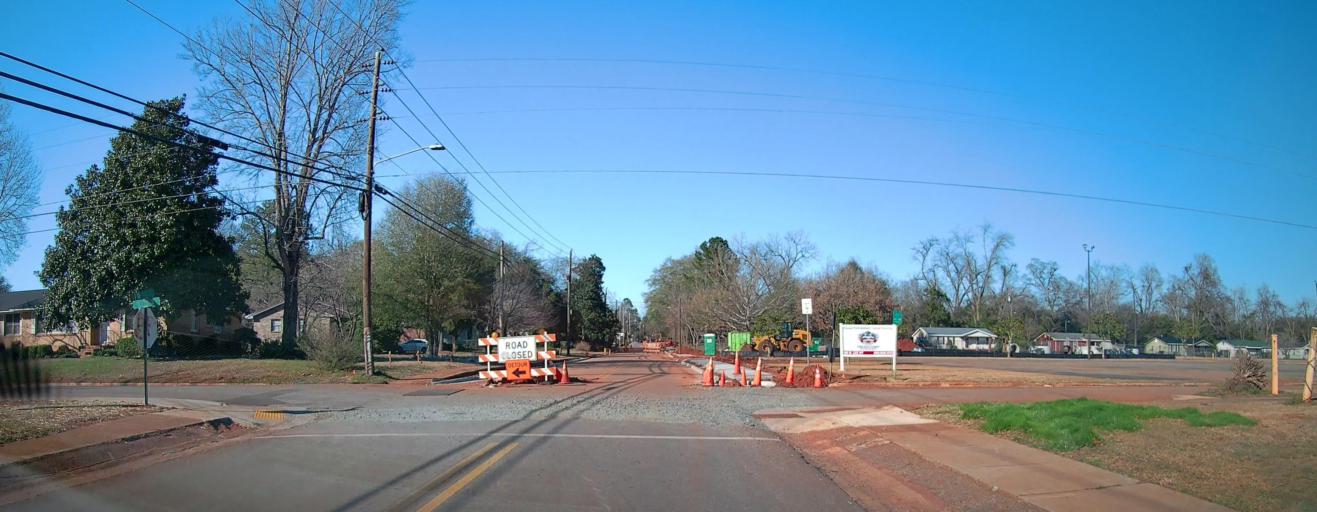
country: US
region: Georgia
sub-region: Sumter County
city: Americus
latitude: 32.0842
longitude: -84.2318
